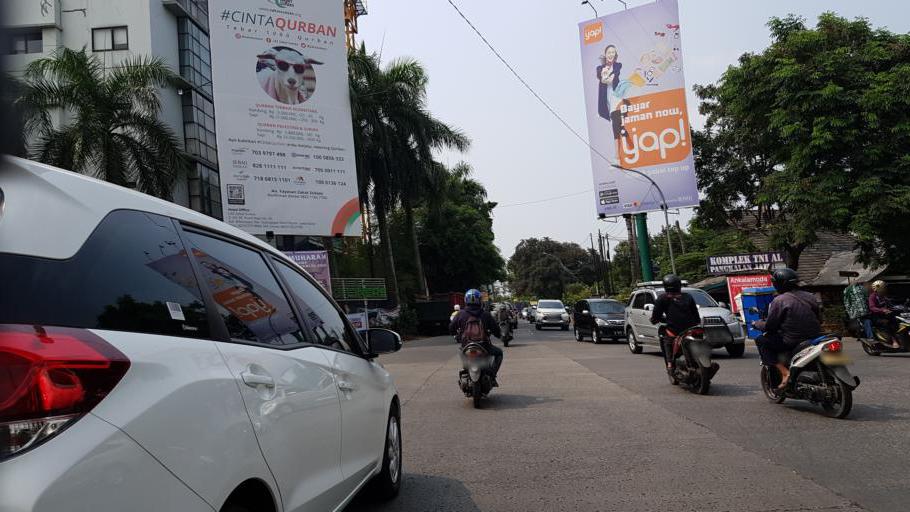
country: ID
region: West Java
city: Pamulang
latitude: -6.3223
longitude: 106.7838
